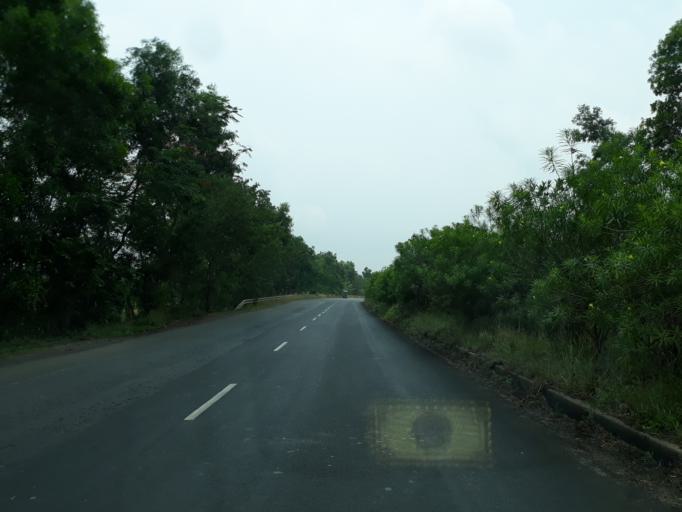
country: IN
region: West Bengal
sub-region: Purba Medinipur
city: Monoharpur
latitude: 22.1001
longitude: 88.0294
